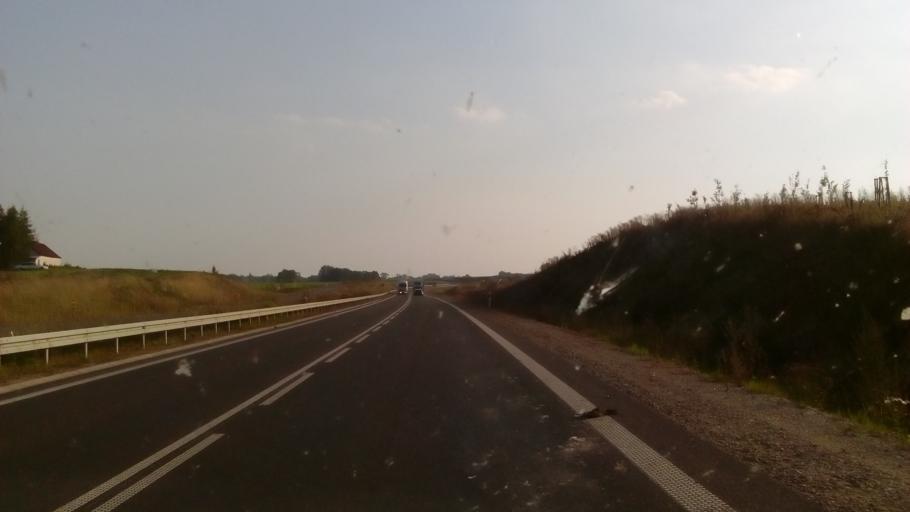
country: PL
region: Podlasie
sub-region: Powiat grajewski
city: Rajgrod
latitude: 53.7733
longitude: 22.8343
